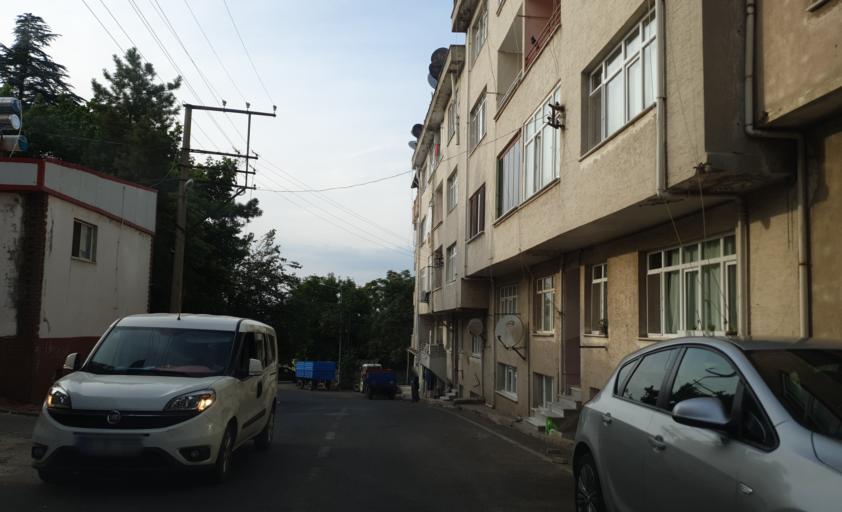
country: TR
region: Tekirdag
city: Hayrabolu
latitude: 41.2168
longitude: 27.1091
